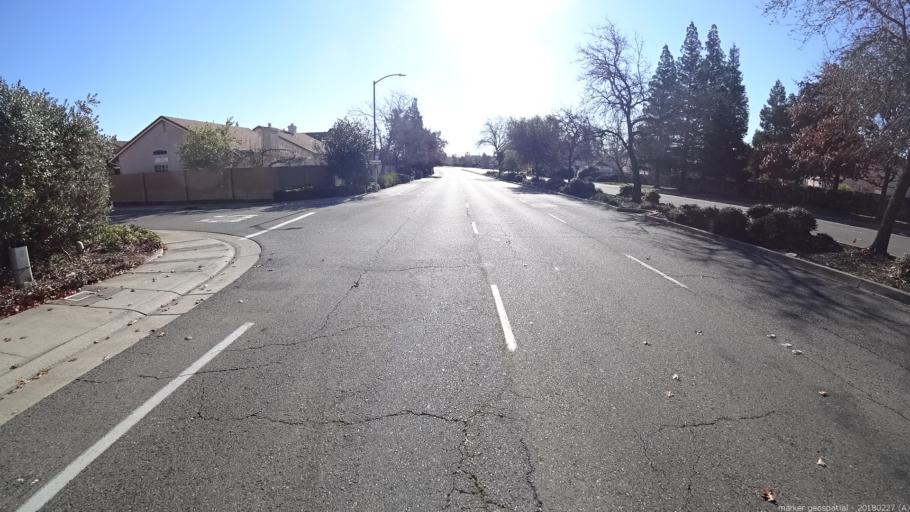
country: US
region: California
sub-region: Sacramento County
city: North Highlands
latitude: 38.7154
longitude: -121.3719
